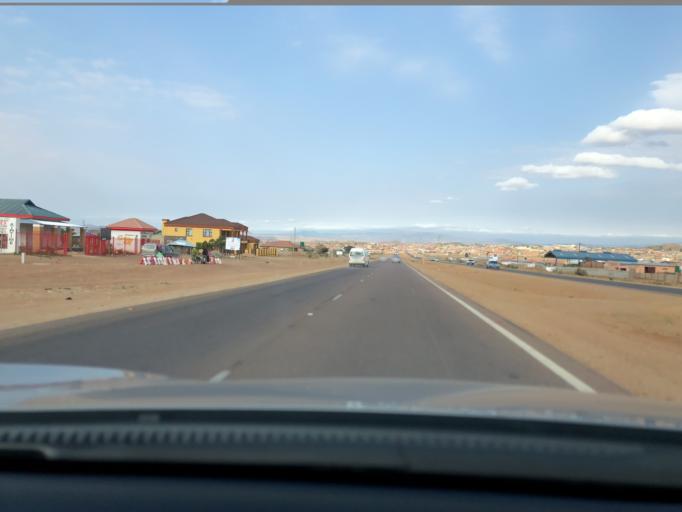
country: ZA
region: Limpopo
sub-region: Capricorn District Municipality
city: Mankoeng
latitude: -23.8882
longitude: 29.6756
